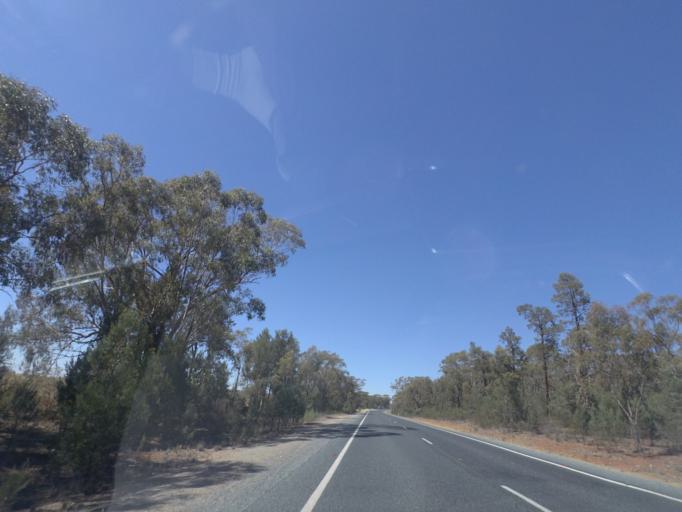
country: AU
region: New South Wales
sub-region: Narrandera
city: Narrandera
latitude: -34.4385
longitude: 146.8418
